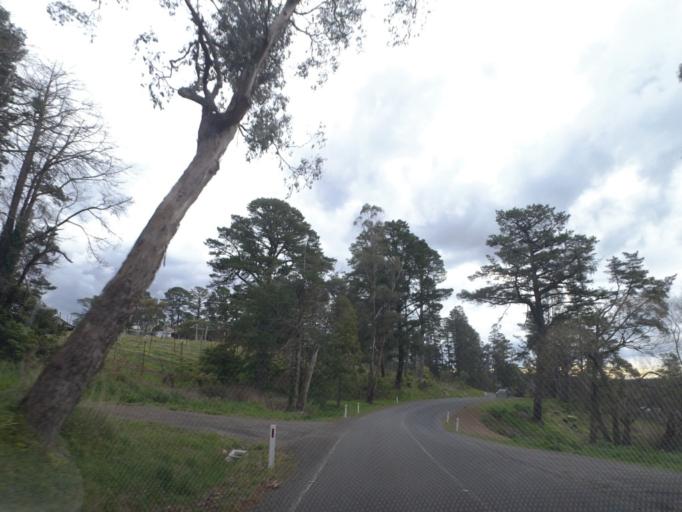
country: AU
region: Victoria
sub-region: Yarra Ranges
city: Mount Evelyn
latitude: -37.7675
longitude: 145.4340
